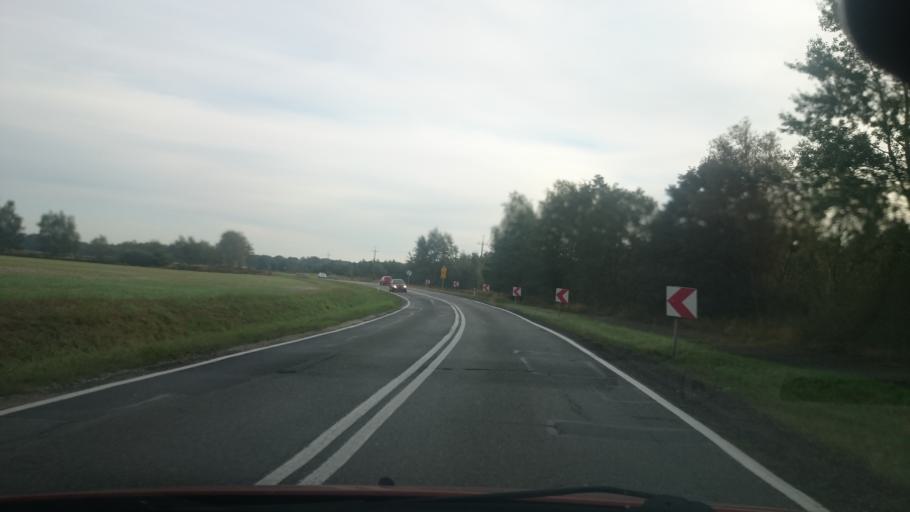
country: PL
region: Lower Silesian Voivodeship
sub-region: Powiat trzebnicki
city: Trzebnica
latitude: 51.3710
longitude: 17.1652
